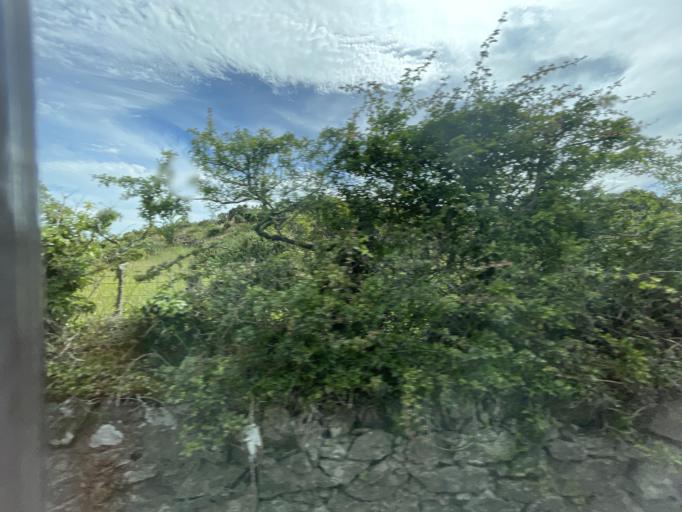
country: GB
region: Wales
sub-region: Anglesey
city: Llanfachraeth
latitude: 53.2613
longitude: -4.4388
